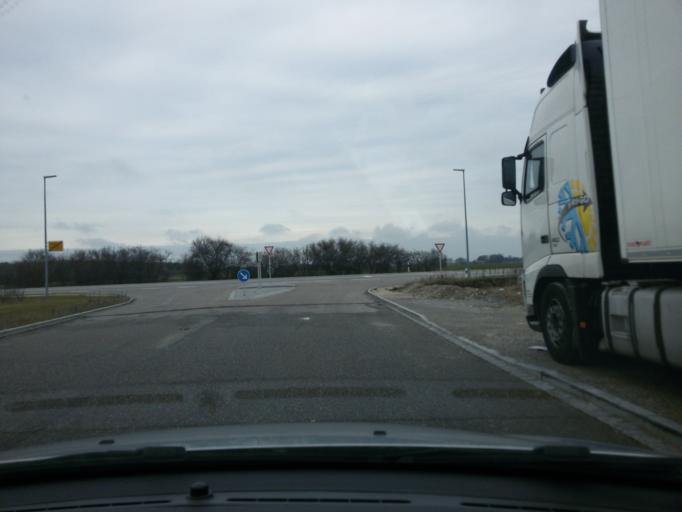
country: DE
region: Bavaria
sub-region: Swabia
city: Kleinaitingen
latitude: 48.2038
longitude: 10.8420
